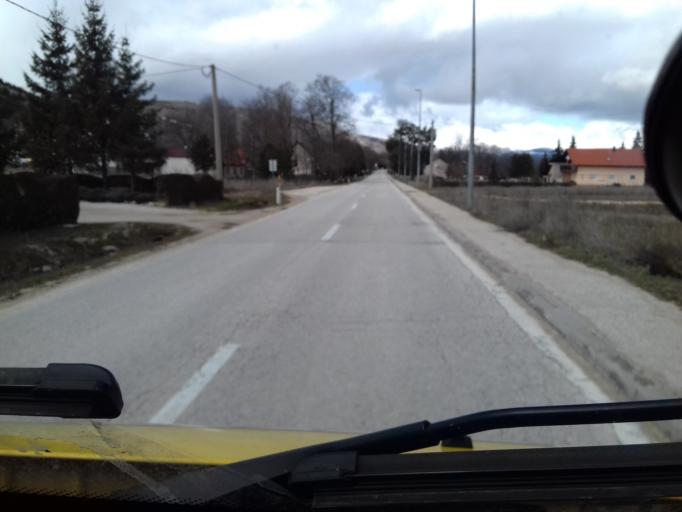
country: BA
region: Federation of Bosnia and Herzegovina
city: Tomislavgrad
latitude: 43.6360
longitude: 17.2402
